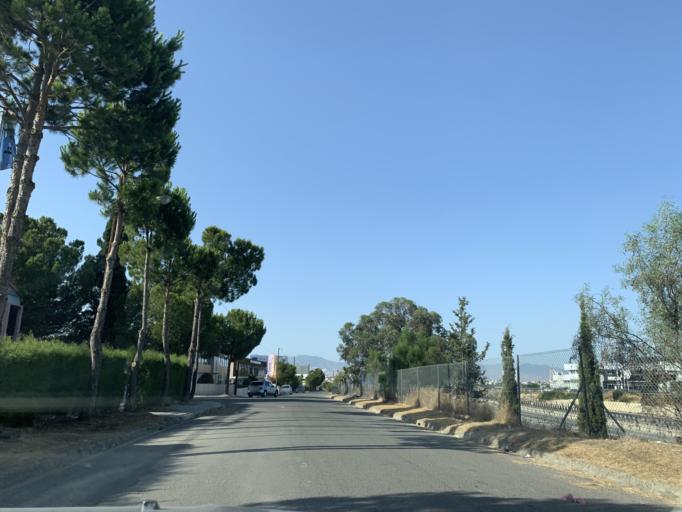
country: CY
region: Lefkosia
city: Nicosia
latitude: 35.1242
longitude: 33.3628
